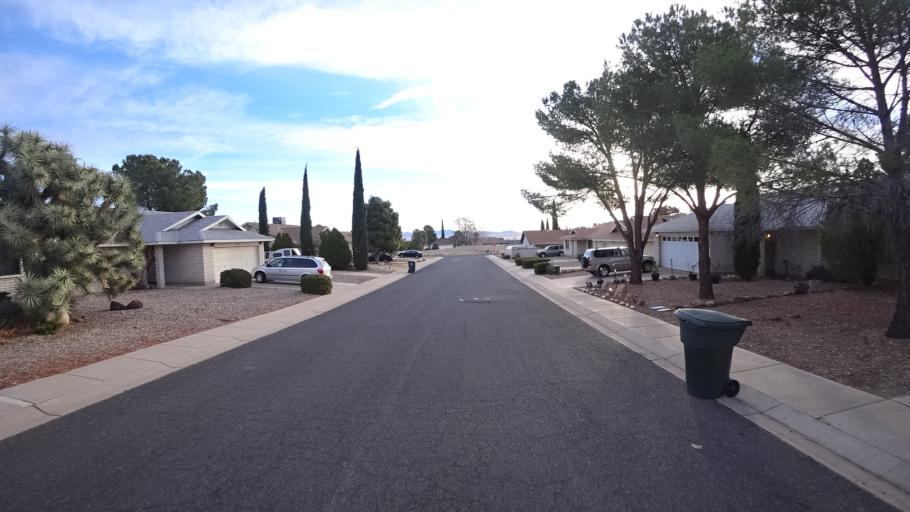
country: US
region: Arizona
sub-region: Mohave County
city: New Kingman-Butler
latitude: 35.2408
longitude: -114.0424
